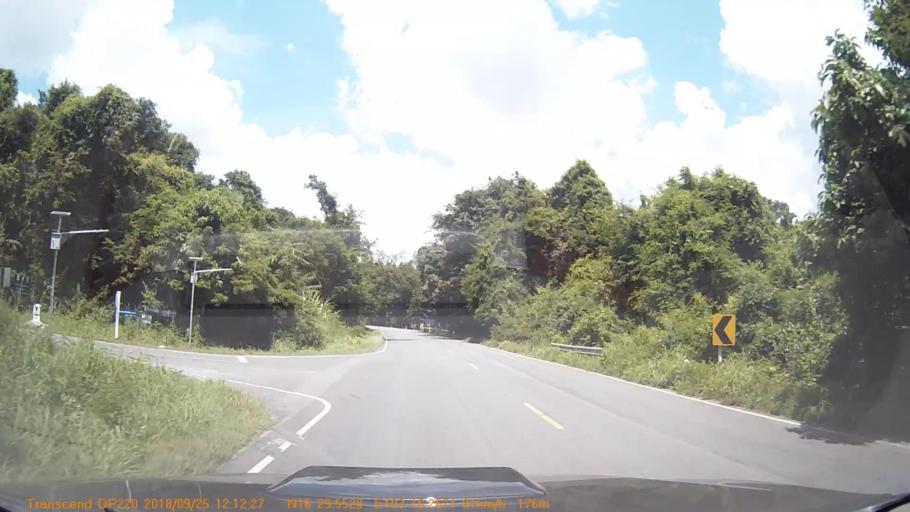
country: TH
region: Kalasin
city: Huai Mek
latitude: 16.4926
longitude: 103.2711
